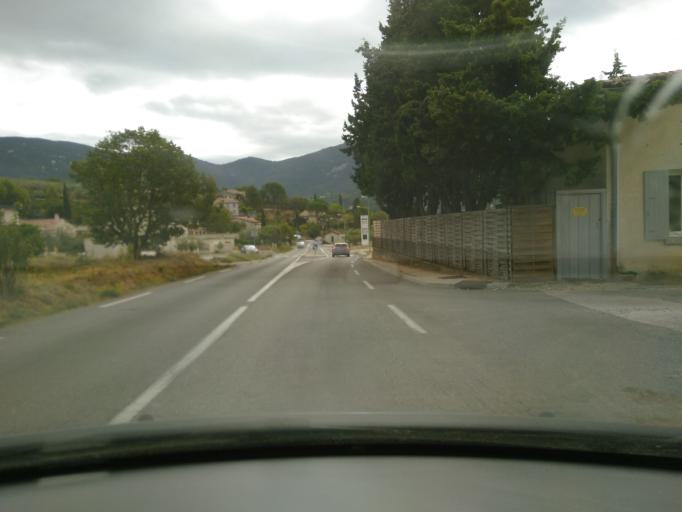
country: FR
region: Rhone-Alpes
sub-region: Departement de la Drome
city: Nyons
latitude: 44.3653
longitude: 5.1253
